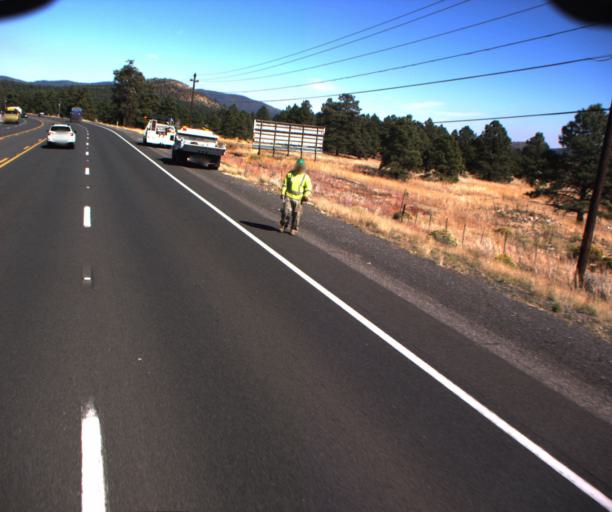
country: US
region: Arizona
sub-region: Coconino County
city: Flagstaff
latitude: 35.2604
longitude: -111.5503
